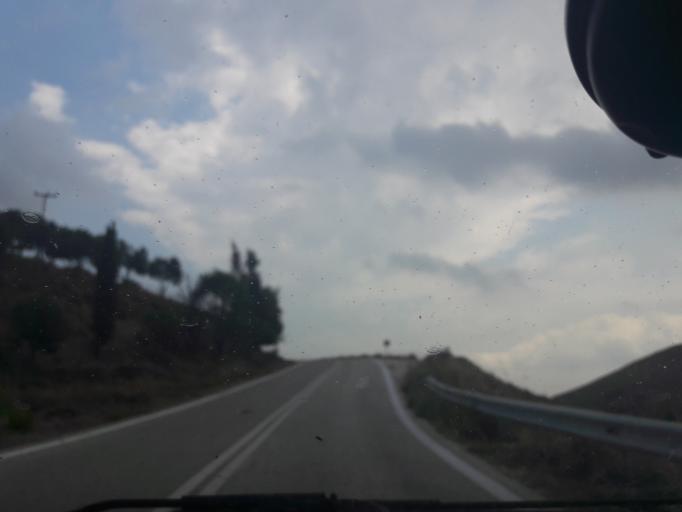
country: GR
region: North Aegean
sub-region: Nomos Lesvou
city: Myrina
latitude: 39.9453
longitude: 25.1623
